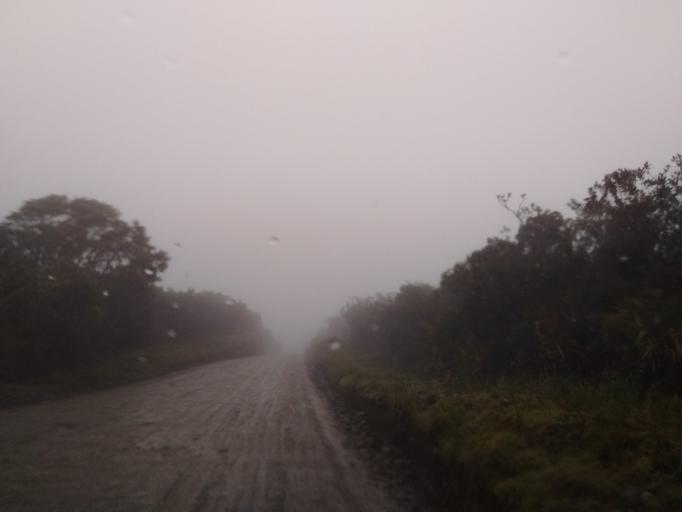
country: CO
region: Cauca
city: Paispamba
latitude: 2.1529
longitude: -76.4218
